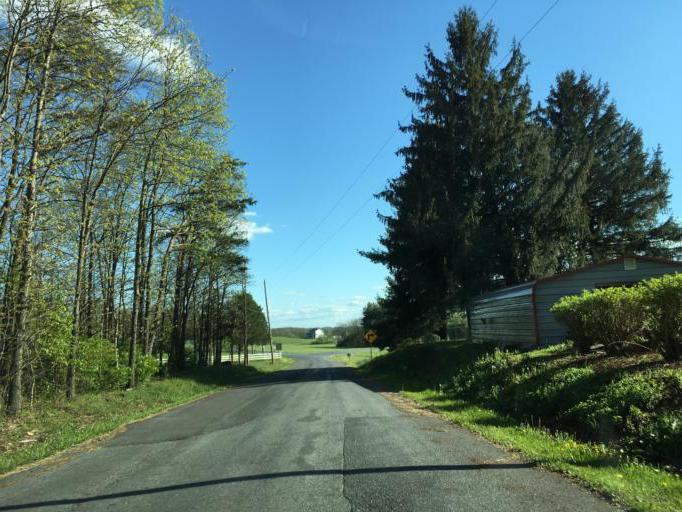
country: US
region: Maryland
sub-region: Frederick County
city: Emmitsburg
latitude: 39.6546
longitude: -77.2823
